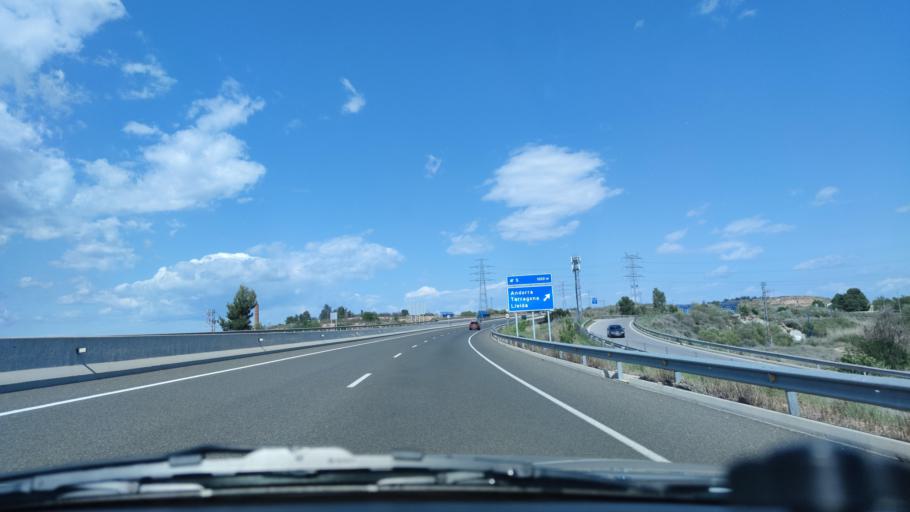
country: ES
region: Catalonia
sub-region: Provincia de Lleida
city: Lleida
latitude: 41.5981
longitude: 0.6507
